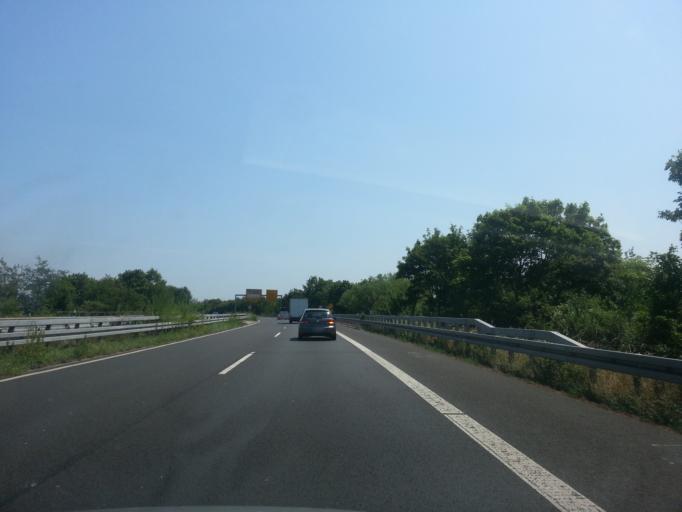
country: DE
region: Hesse
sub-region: Regierungsbezirk Darmstadt
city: Munster
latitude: 49.9084
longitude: 8.8607
